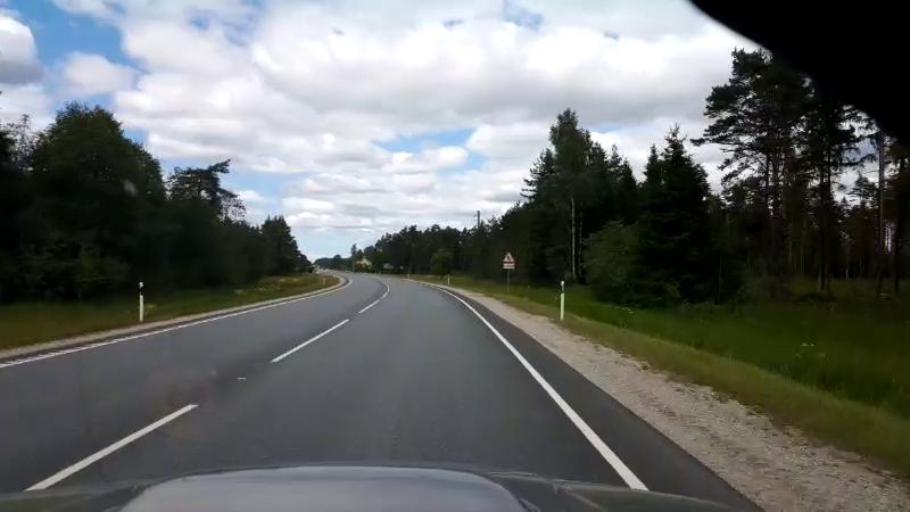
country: EE
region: Raplamaa
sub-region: Maerjamaa vald
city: Marjamaa
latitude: 58.9765
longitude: 24.4746
